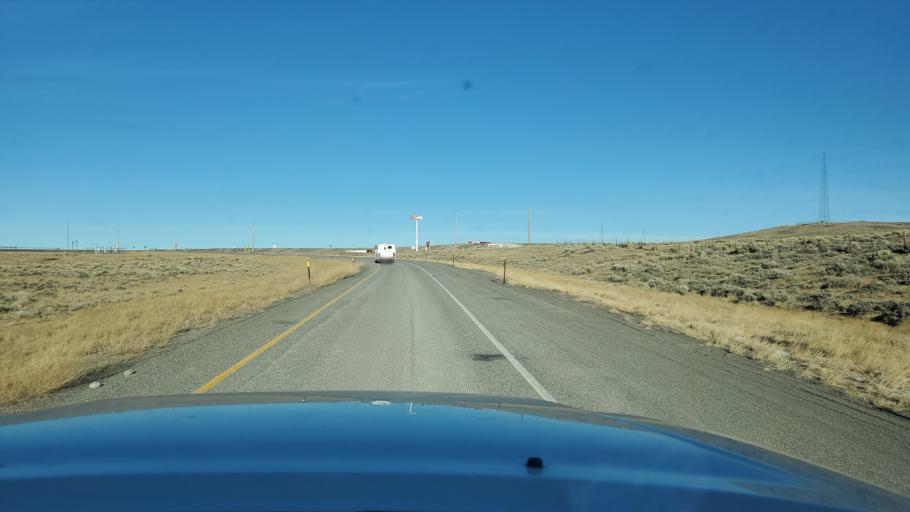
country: US
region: Wyoming
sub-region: Carbon County
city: Saratoga
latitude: 41.7244
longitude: -106.4570
